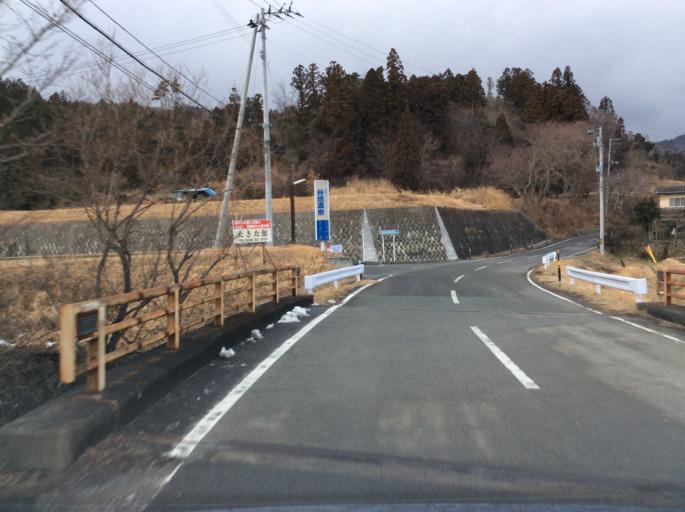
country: JP
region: Fukushima
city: Iwaki
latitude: 37.1801
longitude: 140.9479
